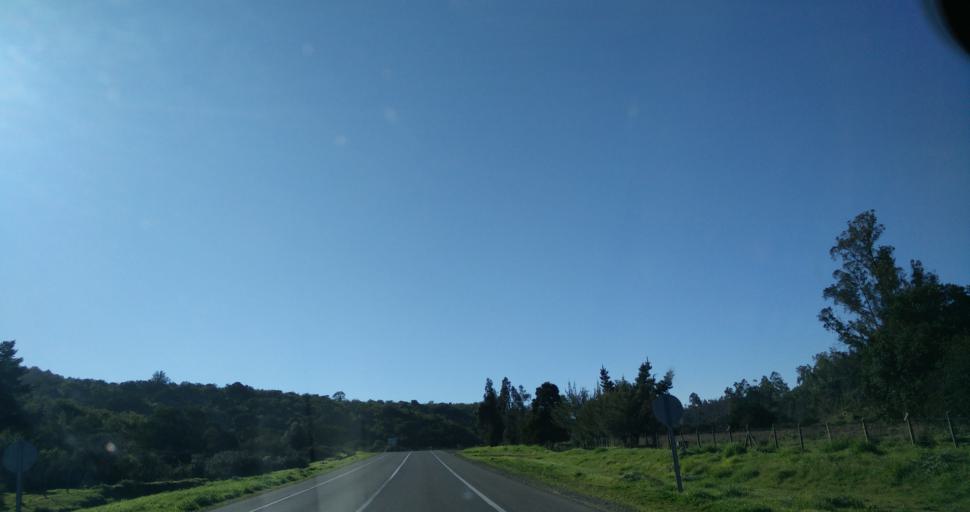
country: CL
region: Valparaiso
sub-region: San Antonio Province
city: Cartagena
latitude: -33.4278
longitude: -71.4486
